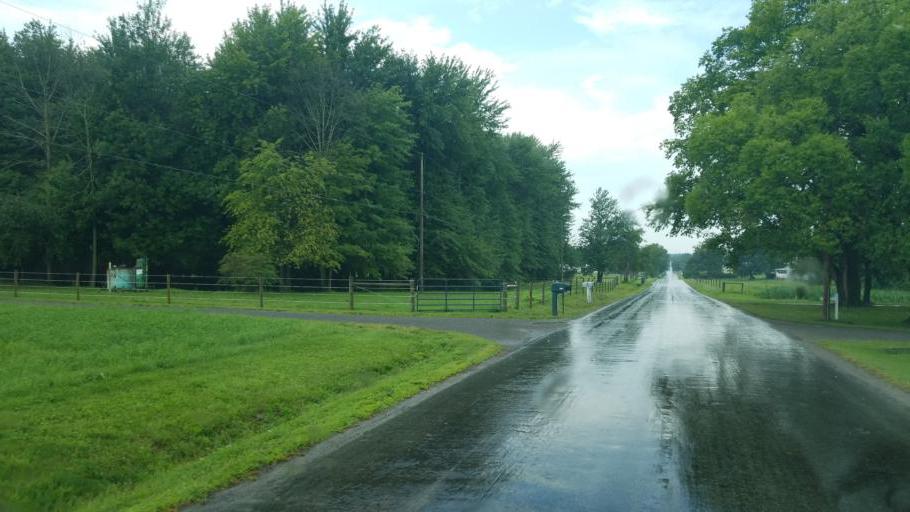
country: US
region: Ohio
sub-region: Geauga County
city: Middlefield
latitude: 41.4761
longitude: -80.9816
